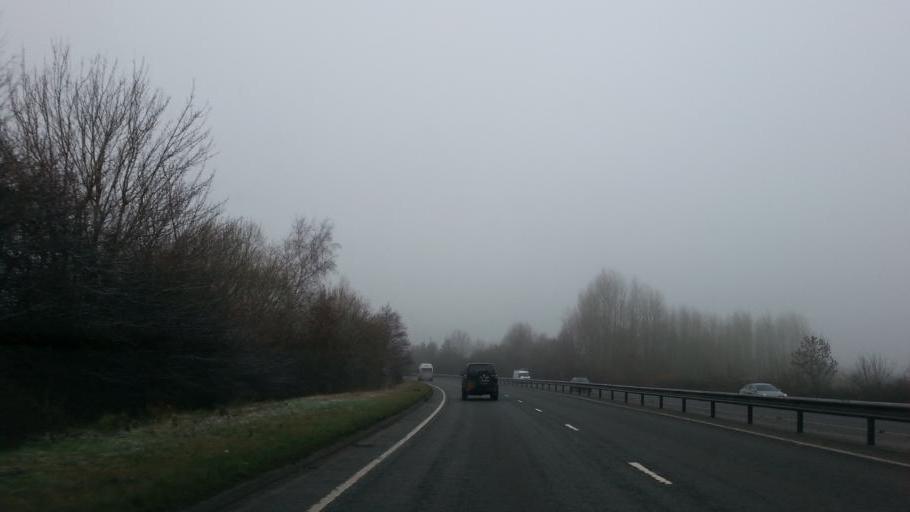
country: GB
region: England
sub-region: Cheshire East
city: Wilmslow
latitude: 53.3167
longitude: -2.2270
